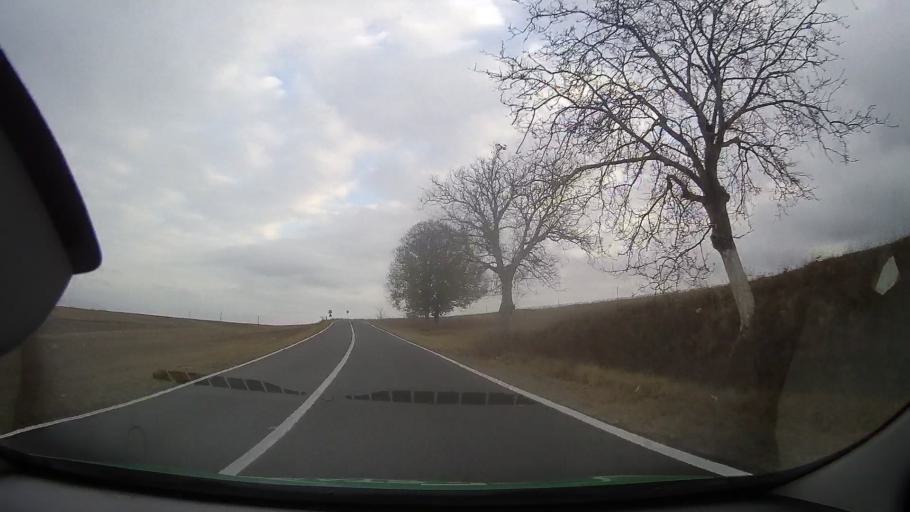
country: RO
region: Constanta
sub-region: Comuna Deleni
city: Deleni
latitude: 44.0950
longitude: 28.0165
